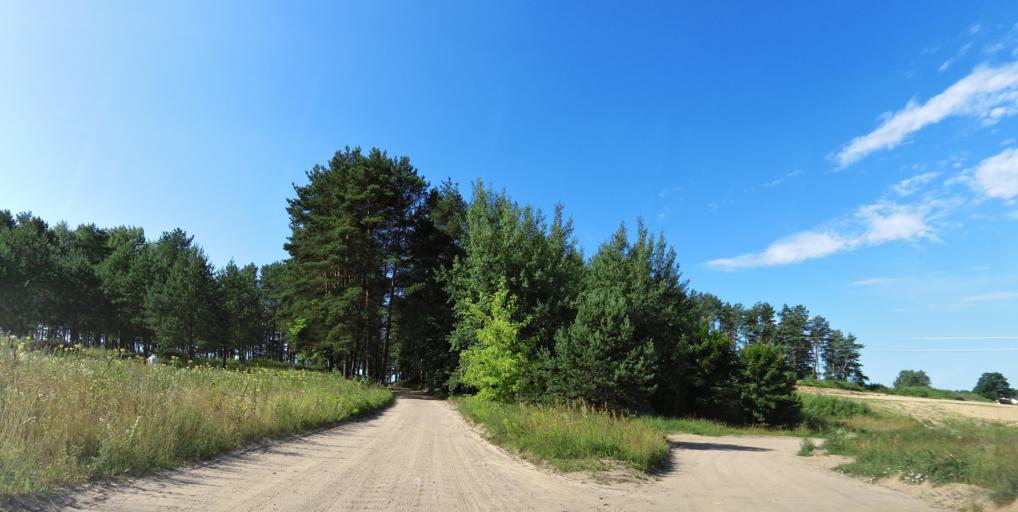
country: LT
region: Vilnius County
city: Pilaite
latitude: 54.6935
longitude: 25.1799
